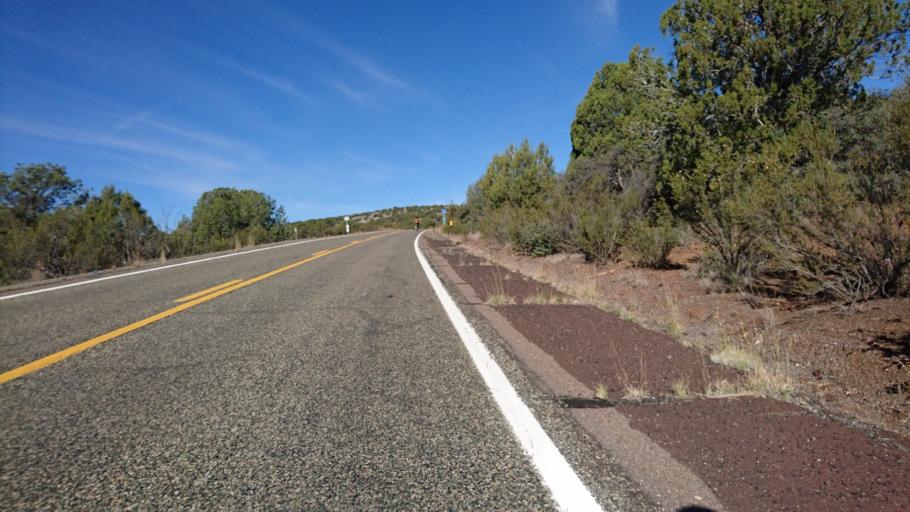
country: US
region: Arizona
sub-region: Yavapai County
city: Paulden
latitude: 35.2729
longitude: -112.6858
